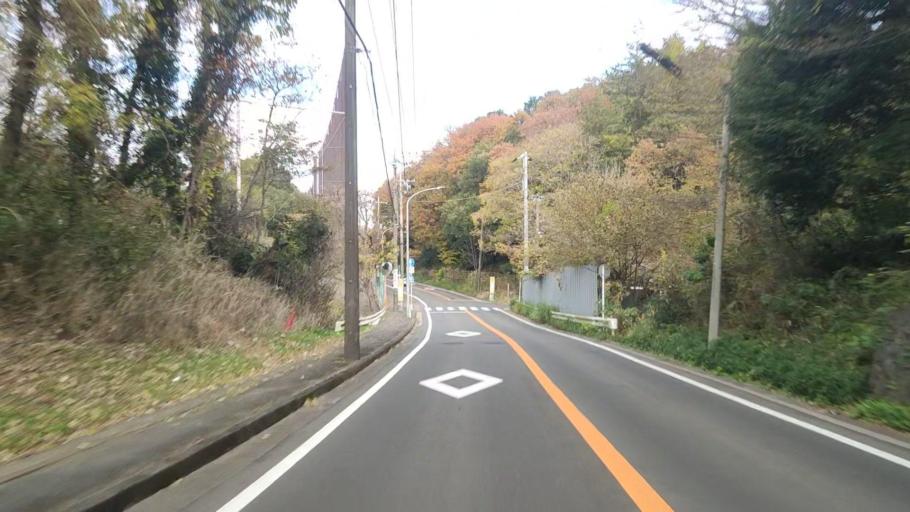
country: JP
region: Kanagawa
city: Minami-rinkan
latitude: 35.4836
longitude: 139.5041
